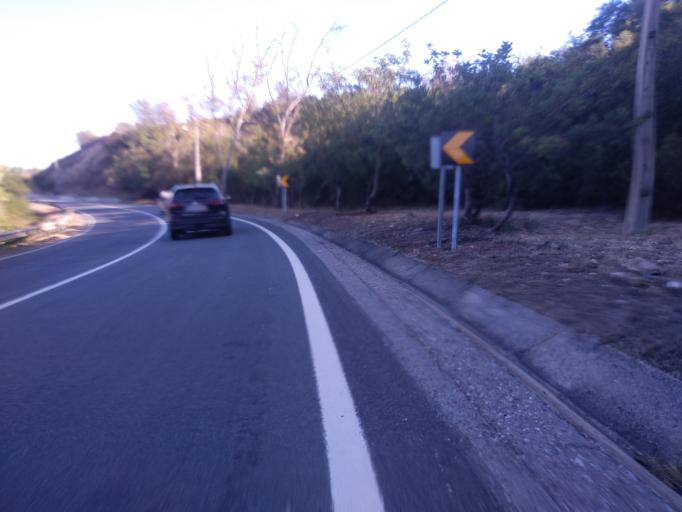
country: PT
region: Faro
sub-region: Sao Bras de Alportel
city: Sao Bras de Alportel
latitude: 37.1047
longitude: -7.9064
